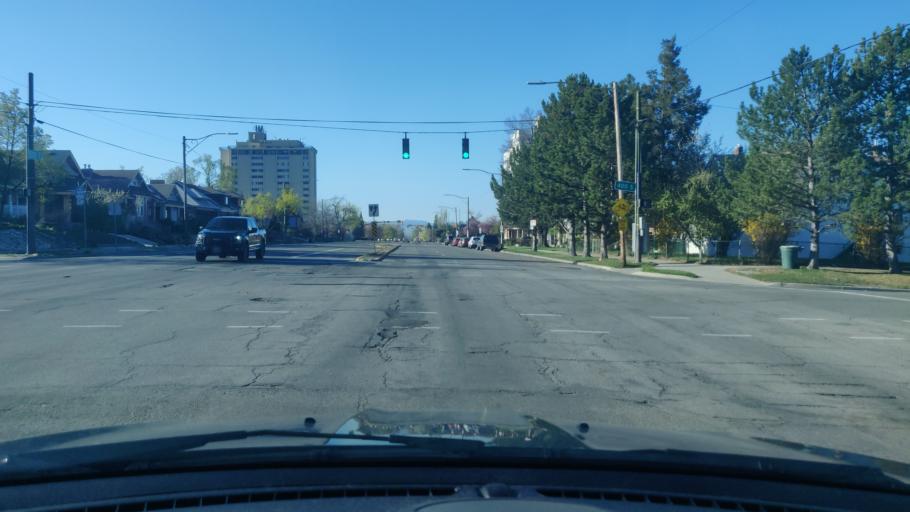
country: US
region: Utah
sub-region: Salt Lake County
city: Salt Lake City
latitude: 40.7608
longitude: -111.8539
